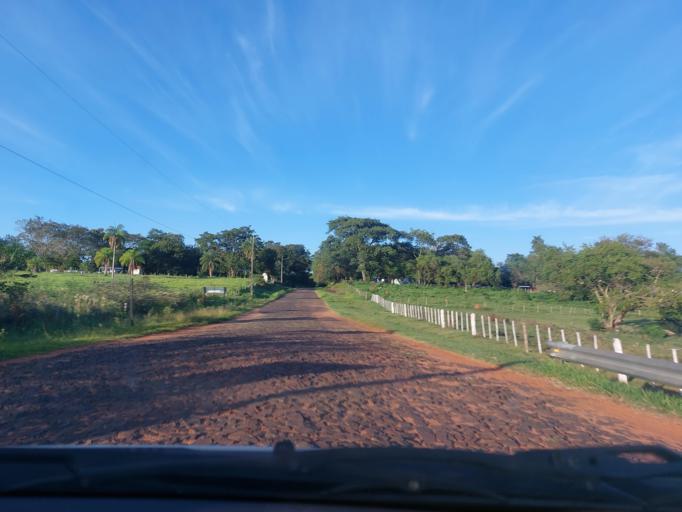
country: PY
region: San Pedro
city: Itacurubi del Rosario
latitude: -24.5669
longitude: -56.5947
